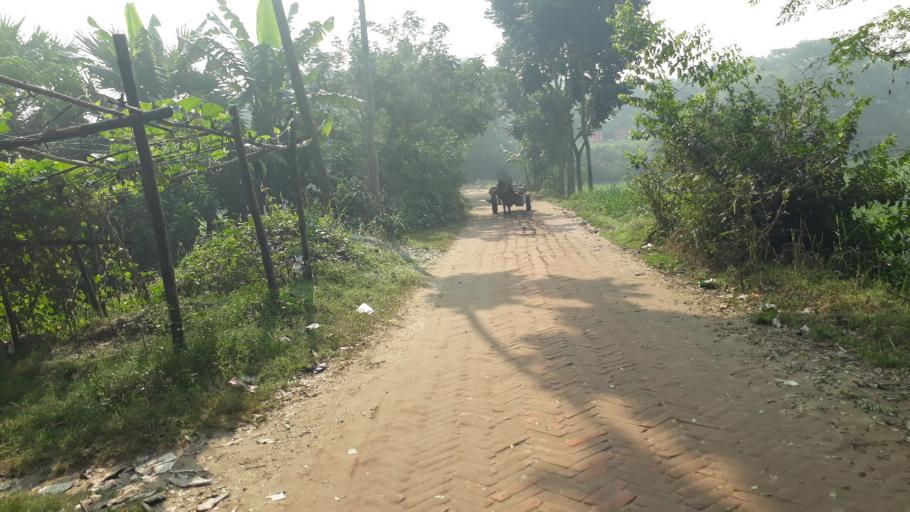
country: BD
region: Dhaka
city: Tungi
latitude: 23.8810
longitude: 90.2581
